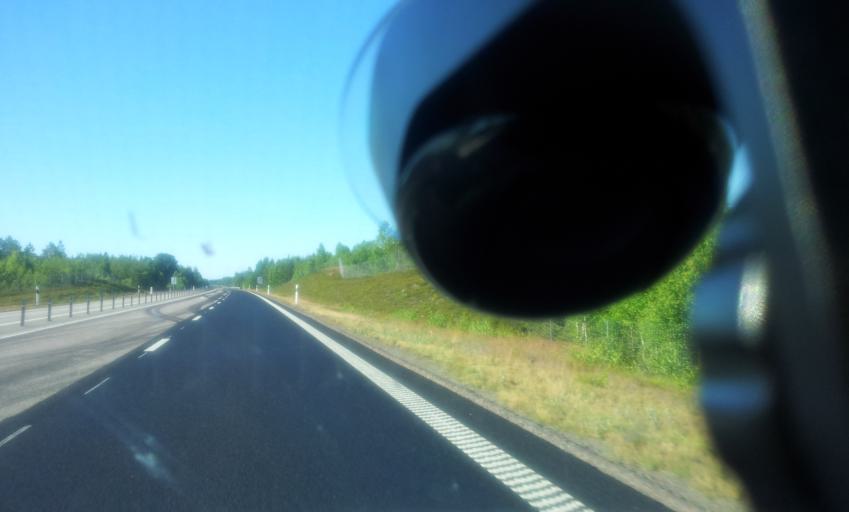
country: SE
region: Kalmar
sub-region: Torsas Kommun
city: Torsas
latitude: 56.4828
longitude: 16.0816
